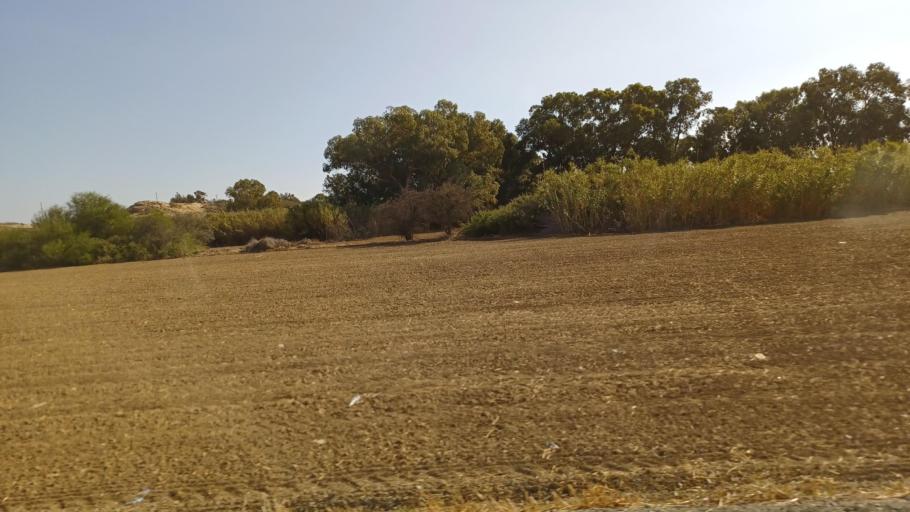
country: CY
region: Larnaka
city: Voroklini
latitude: 34.9901
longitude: 33.6651
